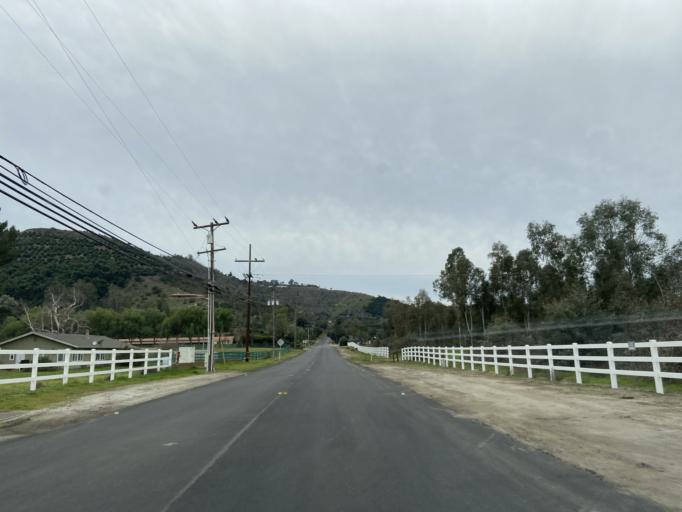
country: US
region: California
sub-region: San Diego County
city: Valley Center
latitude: 33.3116
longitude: -117.0070
